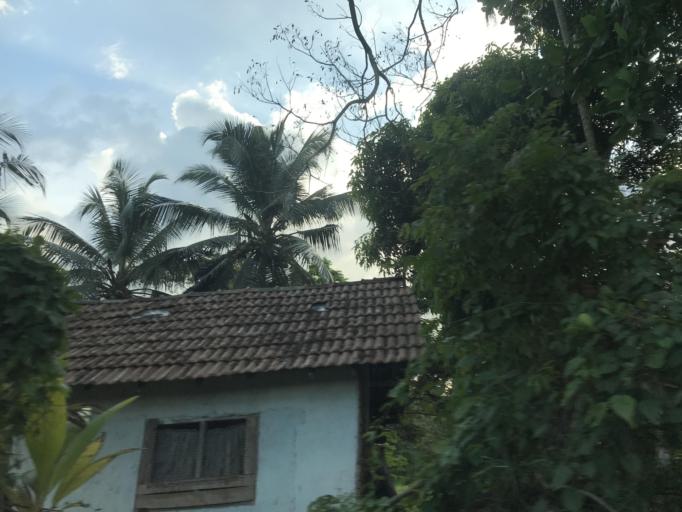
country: LK
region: Western
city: Gampaha
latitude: 7.1022
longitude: 79.9792
